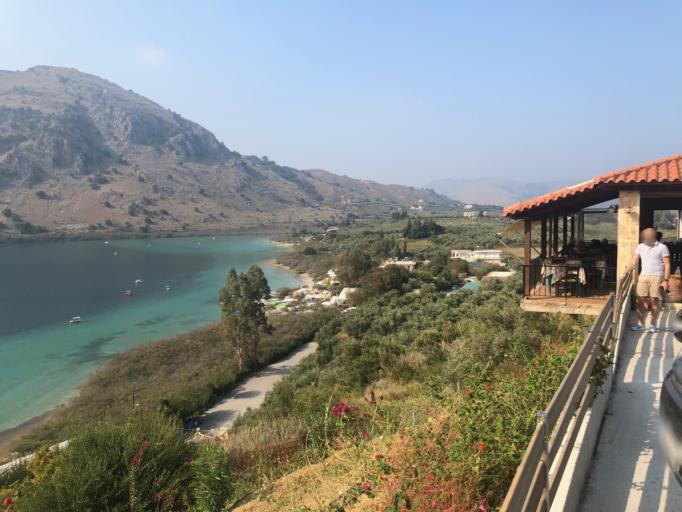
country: GR
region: Crete
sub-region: Nomos Chanias
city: Georgioupolis
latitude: 35.3309
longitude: 24.2813
